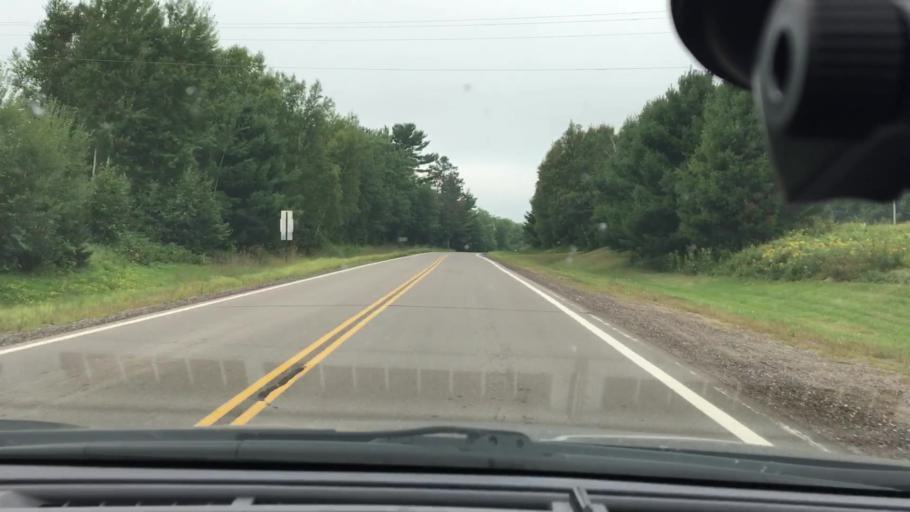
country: US
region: Minnesota
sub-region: Crow Wing County
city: Cross Lake
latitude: 46.6623
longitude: -93.9544
